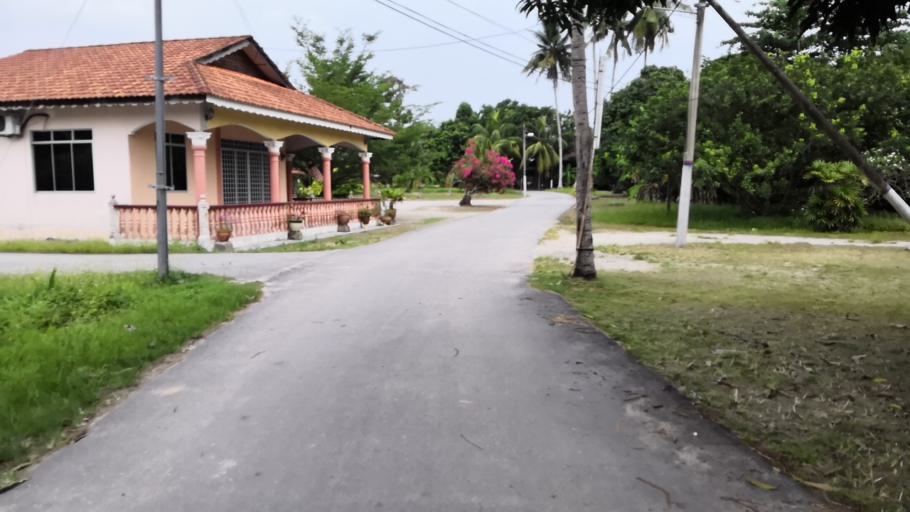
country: MY
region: Perak
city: Lumut
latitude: 4.2975
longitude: 100.6706
